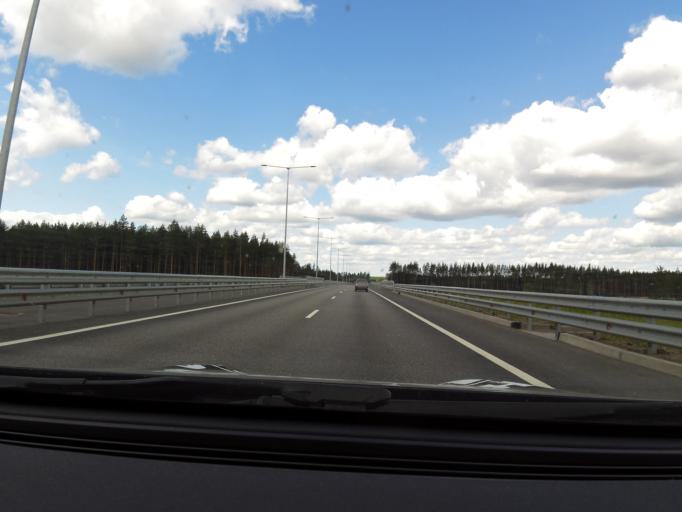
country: RU
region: Tverskaya
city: Krasnomayskiy
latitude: 57.4791
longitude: 34.3317
